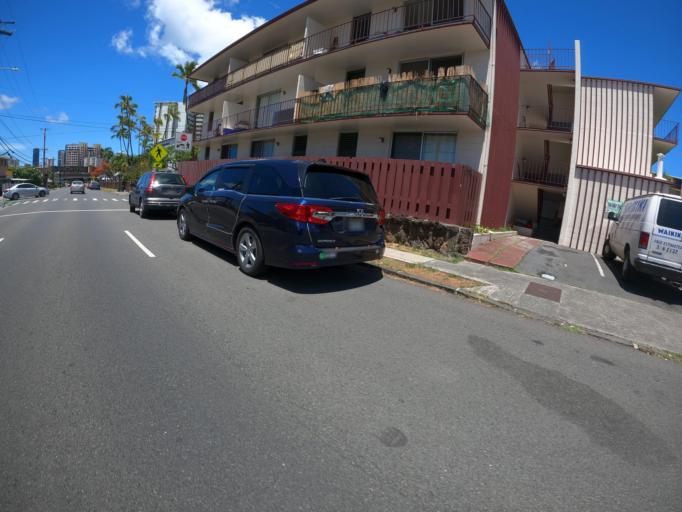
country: US
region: Hawaii
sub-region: Honolulu County
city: Honolulu
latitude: 21.3058
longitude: -157.8428
